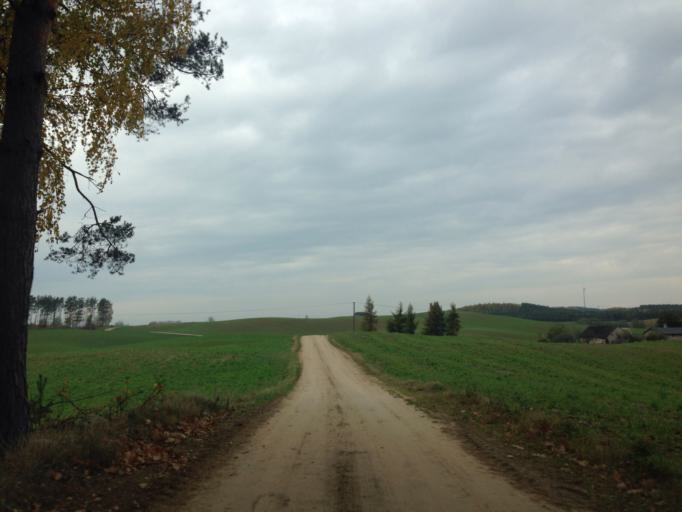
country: PL
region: Kujawsko-Pomorskie
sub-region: Powiat brodnicki
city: Bartniczka
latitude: 53.2679
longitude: 19.6664
